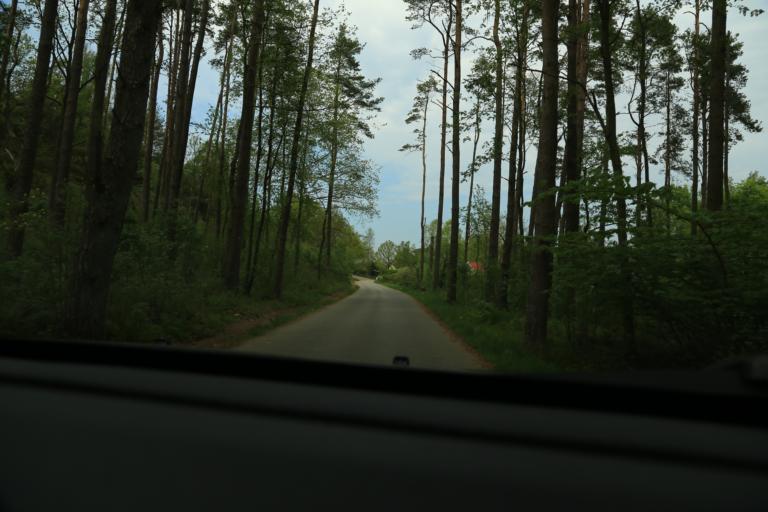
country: SE
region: Halland
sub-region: Varbergs Kommun
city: Varberg
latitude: 57.1479
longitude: 12.2275
